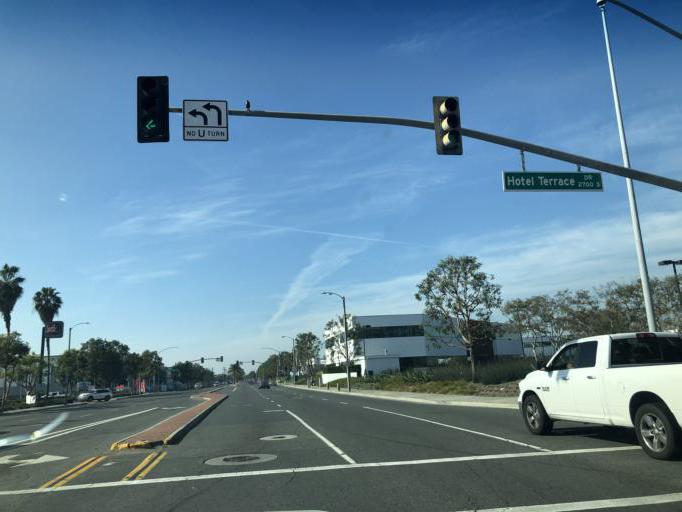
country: US
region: California
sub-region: Orange County
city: Santa Ana
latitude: 33.7087
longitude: -117.8544
